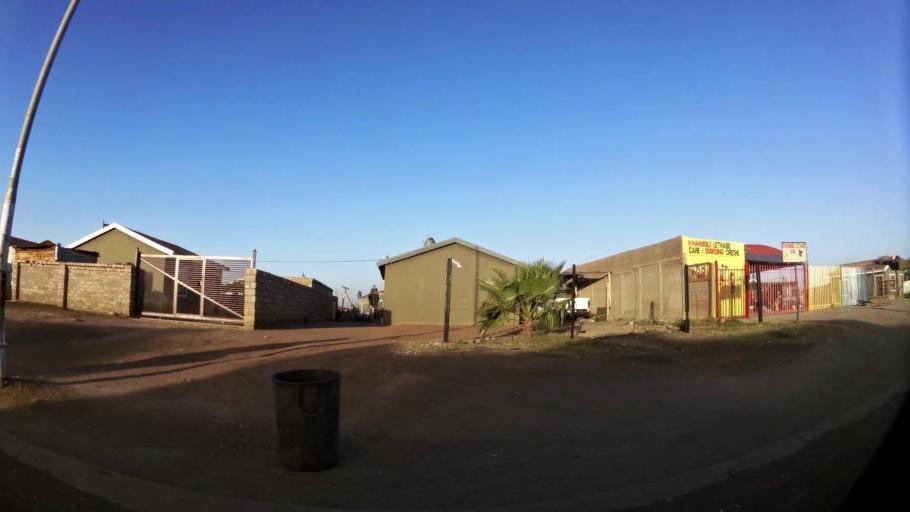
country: ZA
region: North-West
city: Ga-Rankuwa
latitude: -25.5990
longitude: 28.0921
